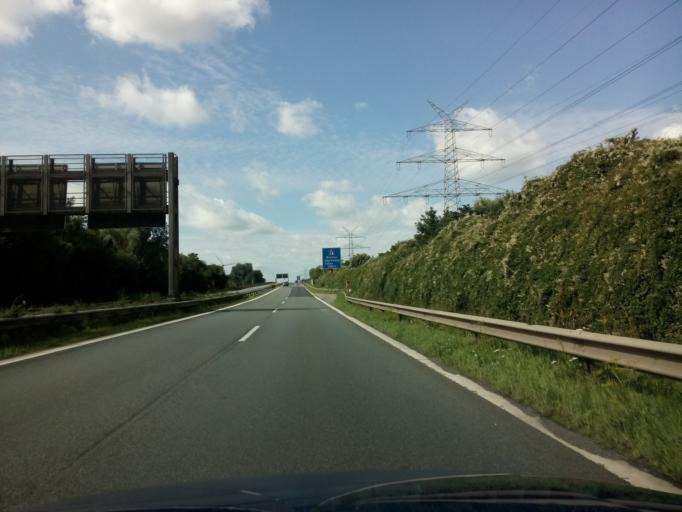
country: DE
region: Lower Saxony
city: Ritterhude
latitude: 53.1454
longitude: 8.7286
